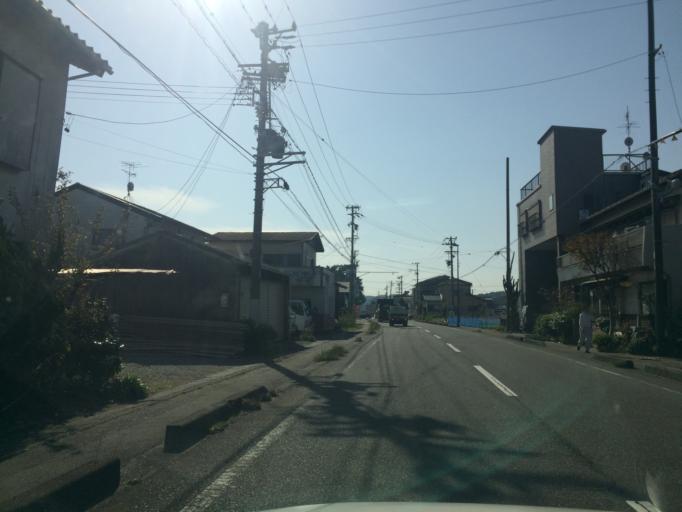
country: JP
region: Shizuoka
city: Sagara
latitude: 34.6810
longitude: 138.2015
